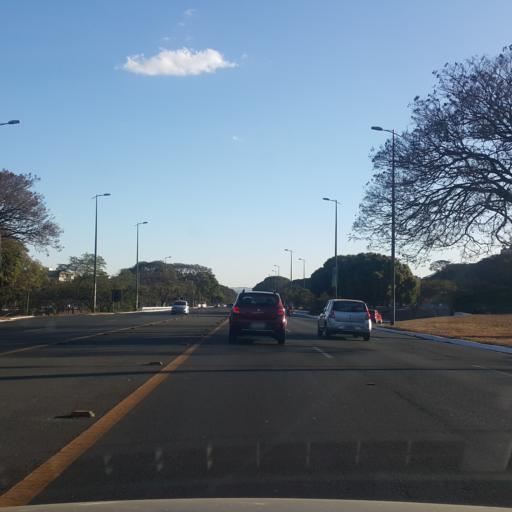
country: BR
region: Federal District
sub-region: Brasilia
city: Brasilia
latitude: -15.8212
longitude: -47.9065
